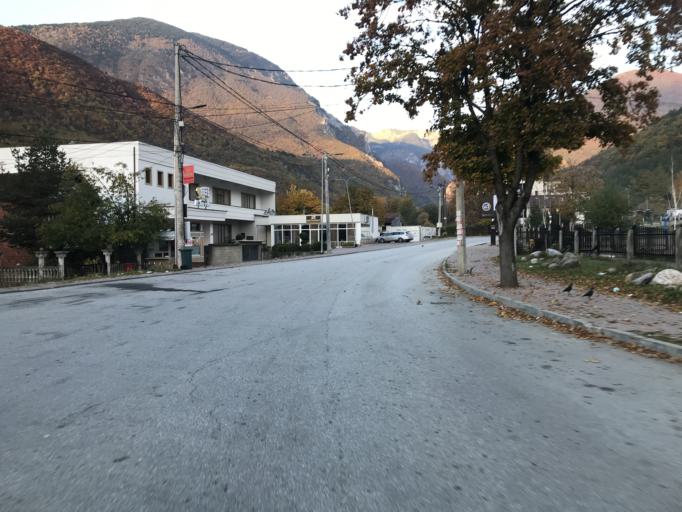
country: XK
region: Pec
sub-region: Komuna e Pejes
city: Peje
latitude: 42.6606
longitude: 20.2733
